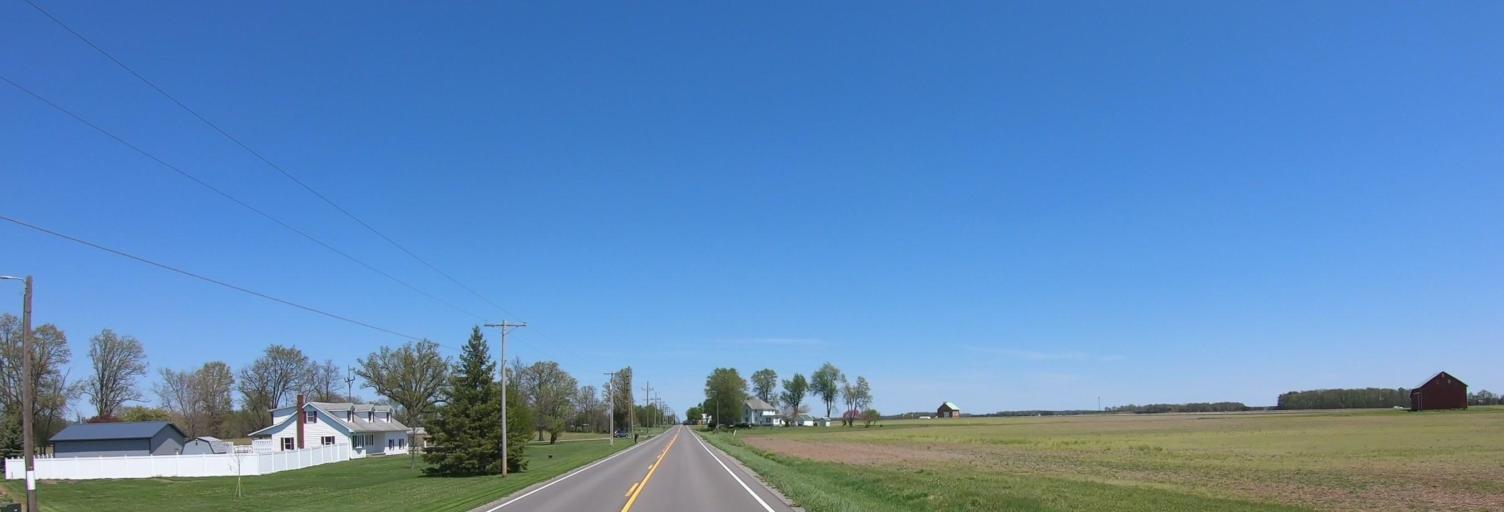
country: US
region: Ohio
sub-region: Allen County
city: Bluffton
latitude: 40.9211
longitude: -83.8281
